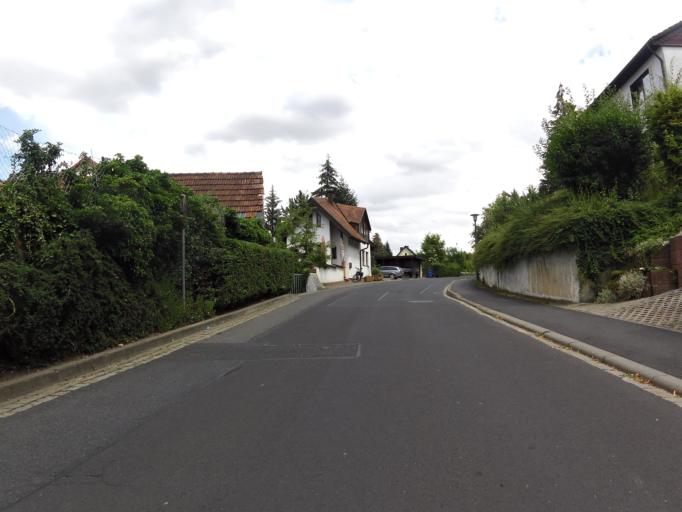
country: DE
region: Bavaria
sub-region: Regierungsbezirk Unterfranken
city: Gerbrunn
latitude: 49.7775
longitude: 9.9892
